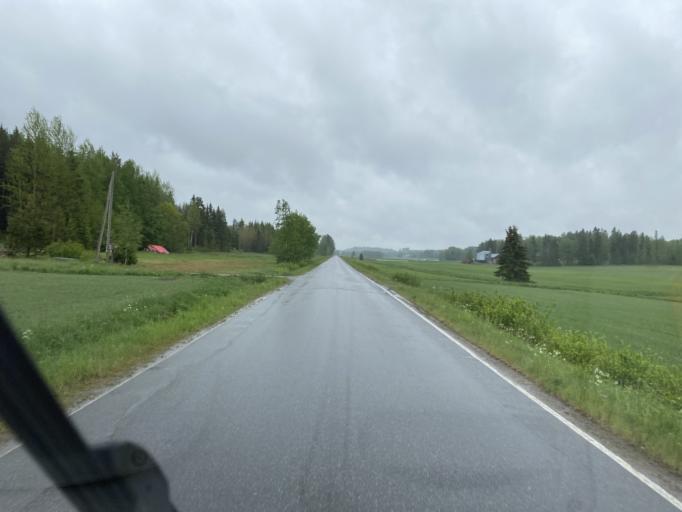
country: FI
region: Haeme
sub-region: Forssa
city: Humppila
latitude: 61.0464
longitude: 23.3746
